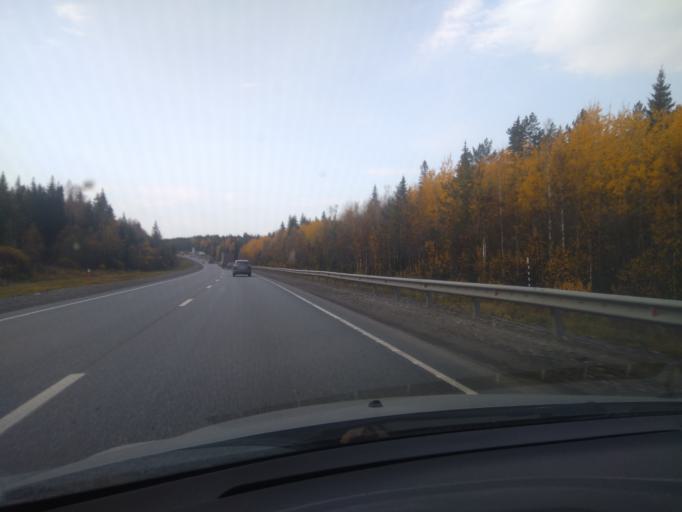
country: RU
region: Sverdlovsk
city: Druzhinino
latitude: 56.8242
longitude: 59.5788
